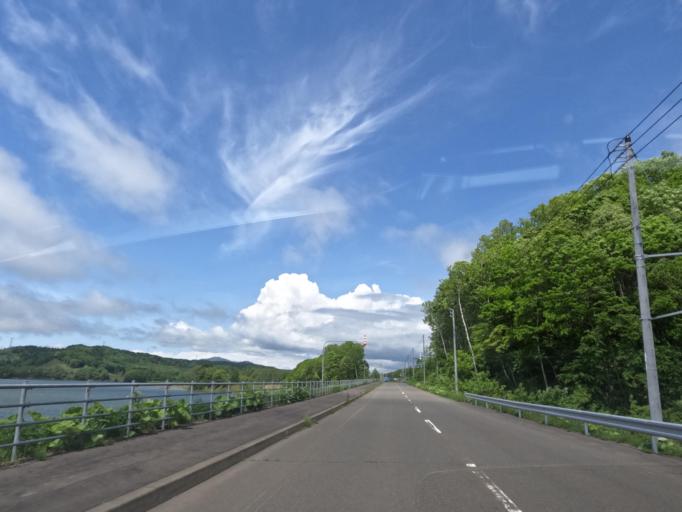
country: JP
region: Hokkaido
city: Tobetsu
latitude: 43.3648
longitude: 141.5720
